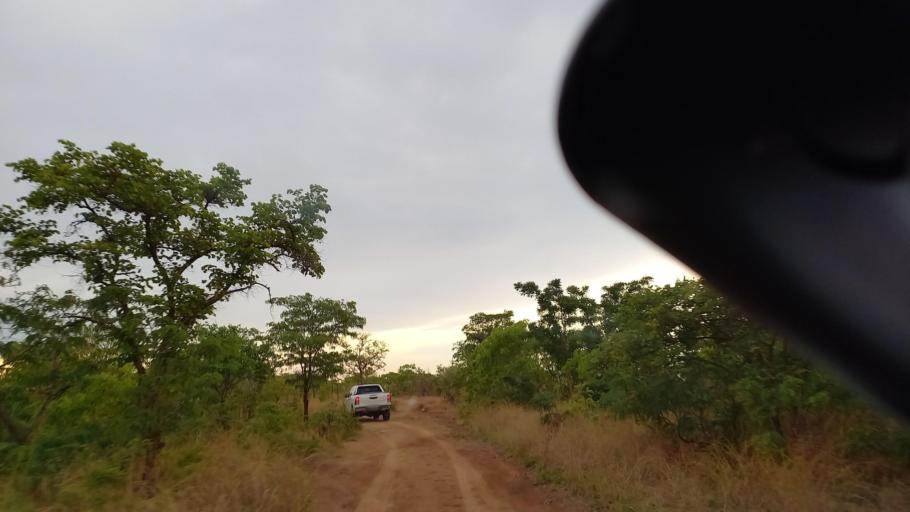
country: ZM
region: Lusaka
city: Kafue
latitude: -16.0485
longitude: 28.3304
